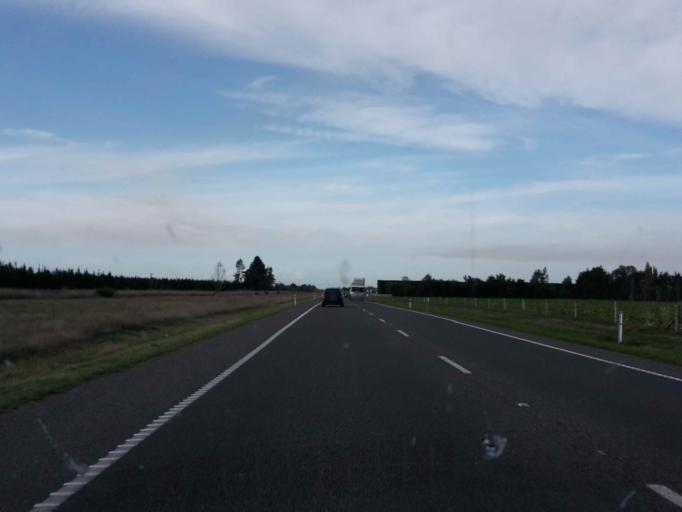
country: NZ
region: Canterbury
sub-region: Ashburton District
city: Tinwald
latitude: -43.9657
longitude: 171.6364
